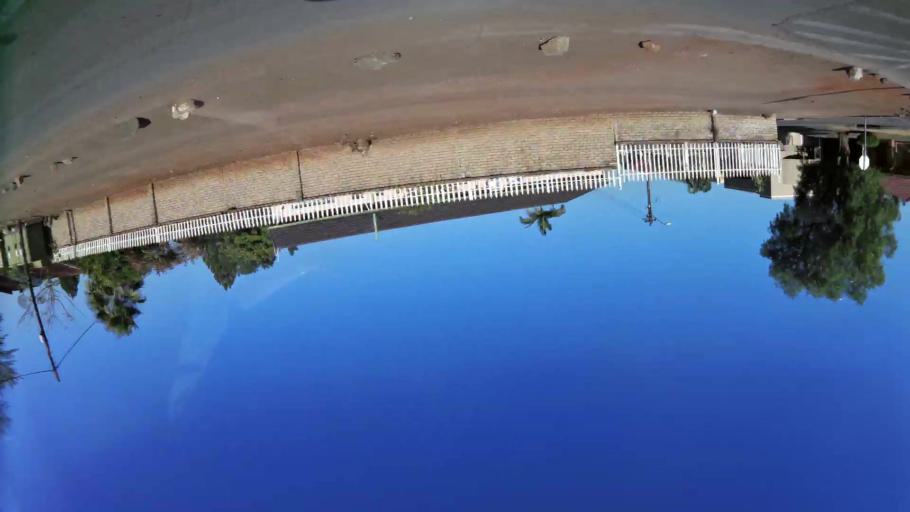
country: ZA
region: North-West
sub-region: Bojanala Platinum District Municipality
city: Rustenburg
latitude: -25.6482
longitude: 27.2434
